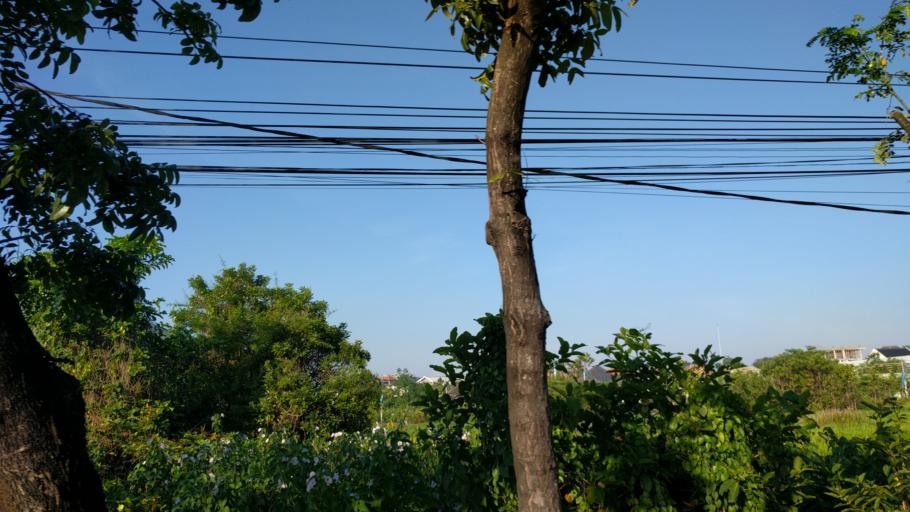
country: ID
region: Bali
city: Kuta
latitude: -8.6936
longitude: 115.1745
